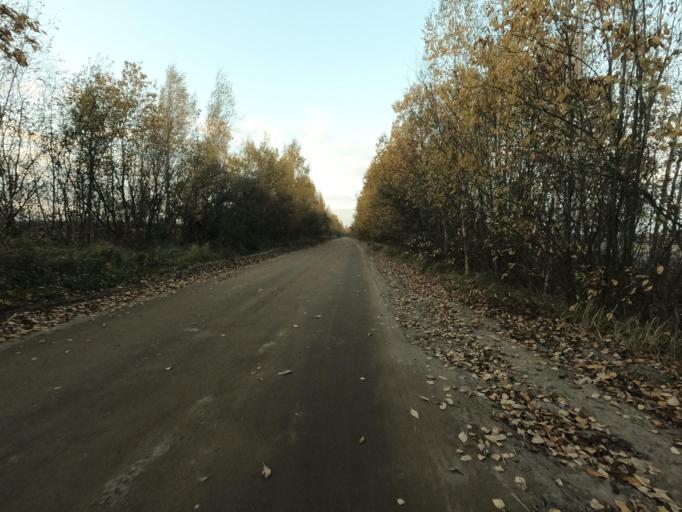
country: RU
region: Leningrad
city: Mga
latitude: 59.7945
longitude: 31.2007
